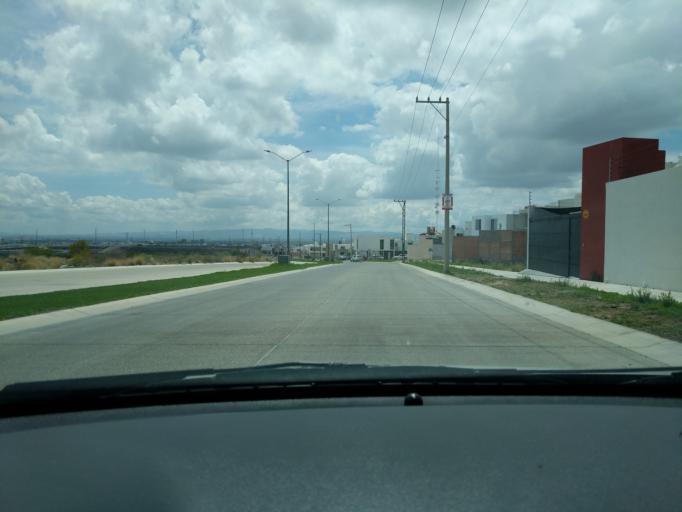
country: MX
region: San Luis Potosi
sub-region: Mexquitic de Carmona
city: Guadalupe Victoria
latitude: 22.1610
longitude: -101.0540
